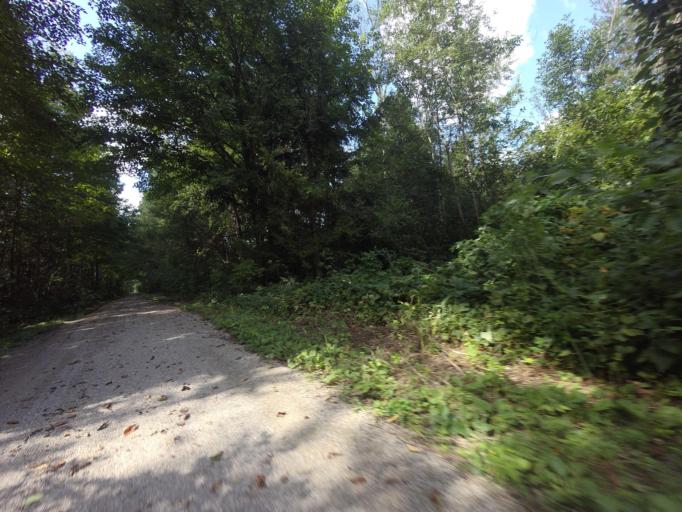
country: CA
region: Ontario
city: Huron East
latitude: 43.6765
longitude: -81.2905
